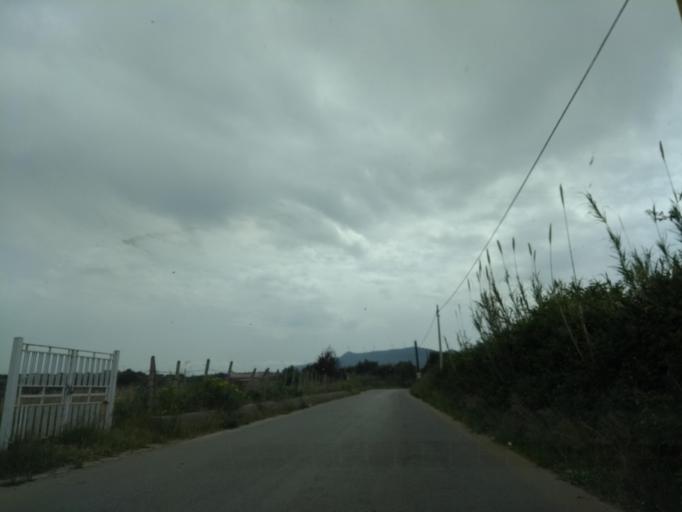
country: IT
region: Sicily
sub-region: Palermo
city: Partinico
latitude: 38.0055
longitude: 13.0679
